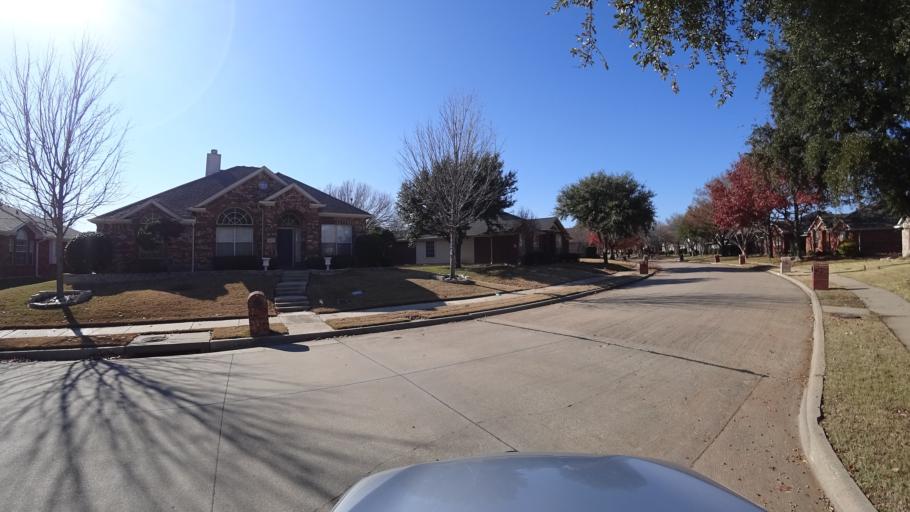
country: US
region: Texas
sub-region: Denton County
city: Lewisville
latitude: 33.0124
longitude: -97.0250
